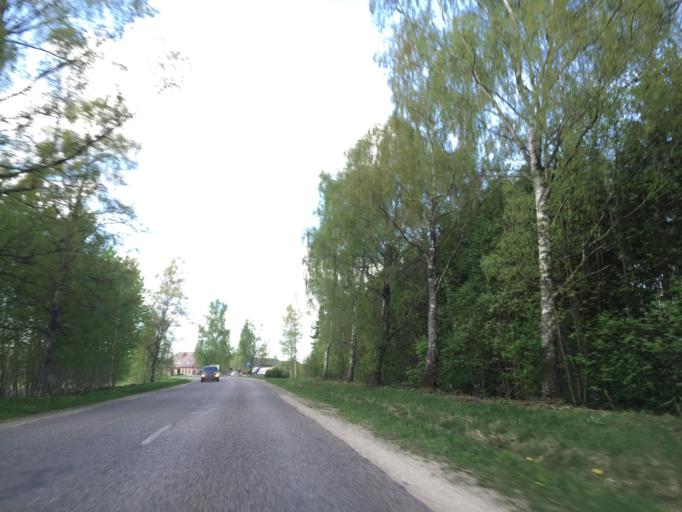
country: LV
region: Limbazu Rajons
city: Limbazi
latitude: 57.4842
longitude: 24.7105
